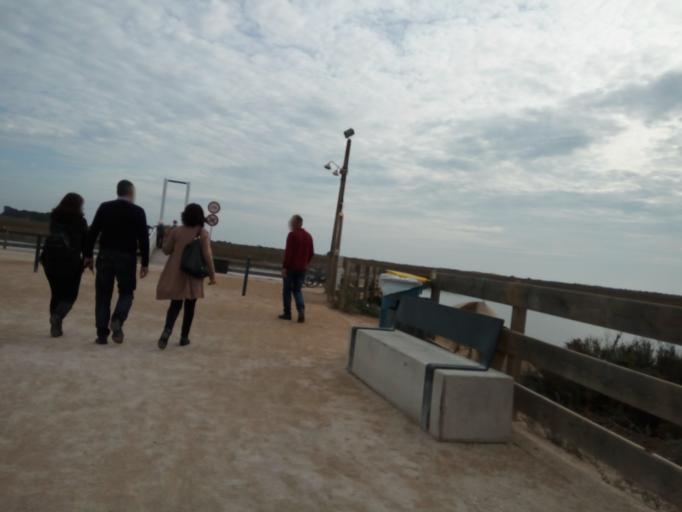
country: PT
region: Faro
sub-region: Tavira
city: Luz
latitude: 37.0922
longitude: -7.6742
